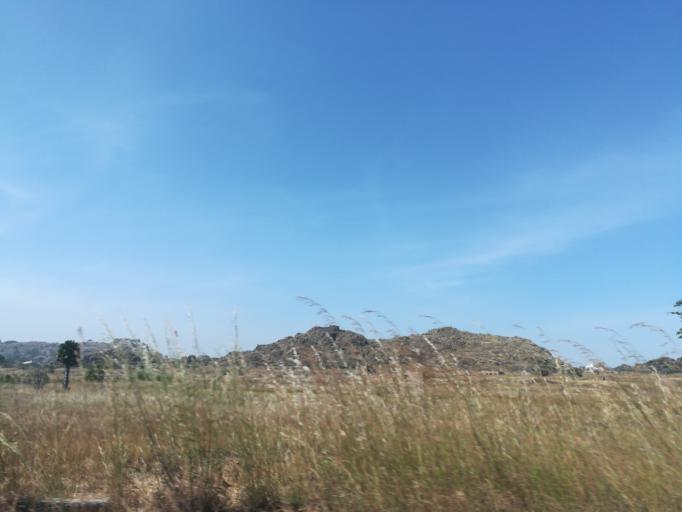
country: NG
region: Plateau
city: Bukuru
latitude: 9.7684
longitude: 8.9017
